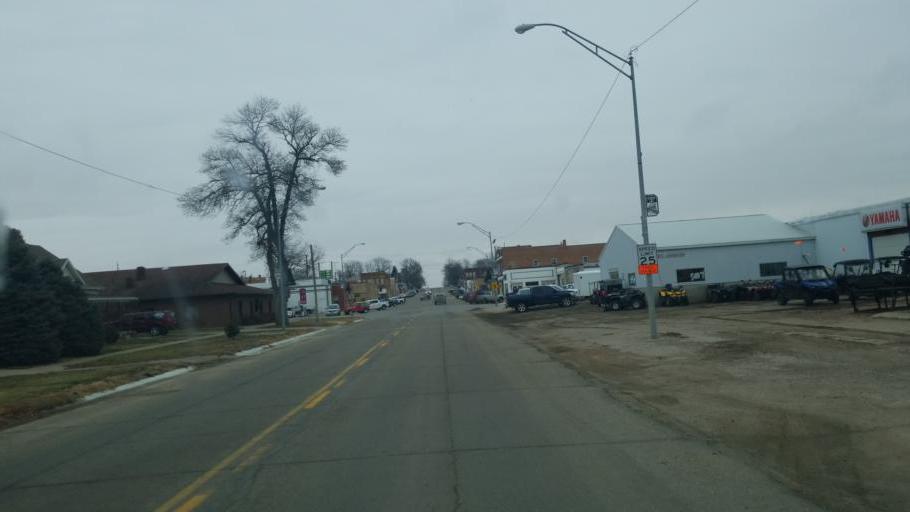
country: US
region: Nebraska
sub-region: Knox County
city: Bloomfield
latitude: 42.5992
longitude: -97.6482
